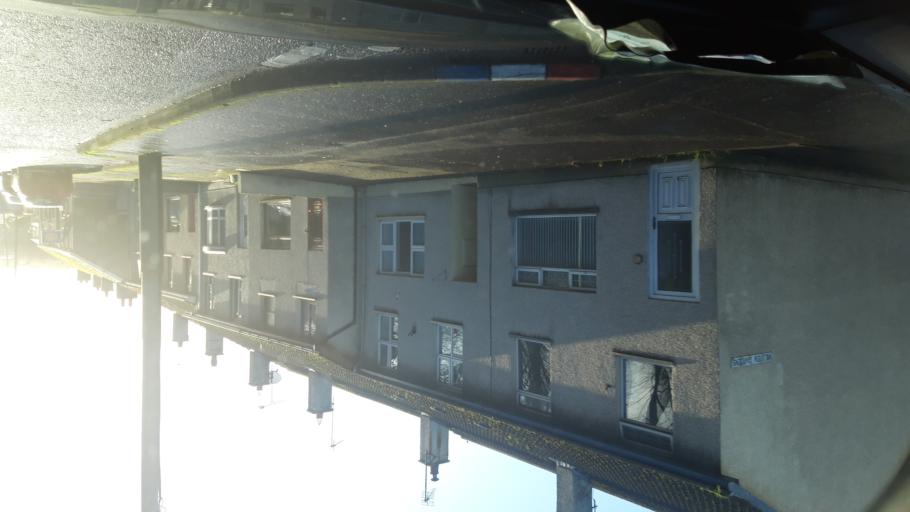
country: GB
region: Northern Ireland
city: Garvagh
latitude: 54.9814
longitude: -6.6880
